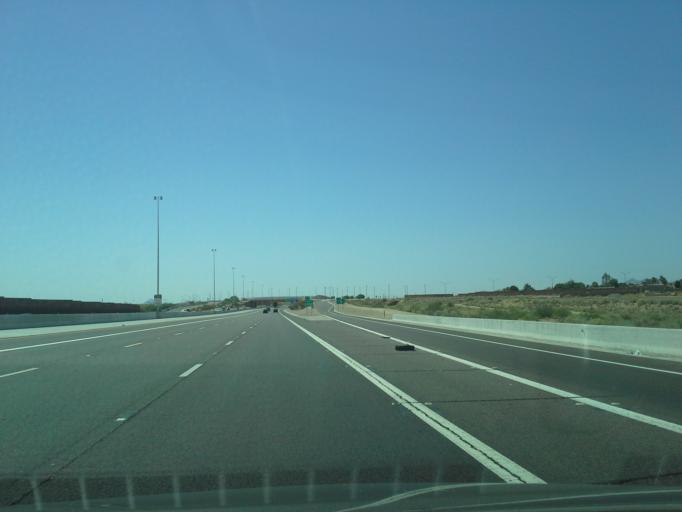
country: US
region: Arizona
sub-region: Pinal County
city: Apache Junction
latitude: 33.4336
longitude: -111.6429
